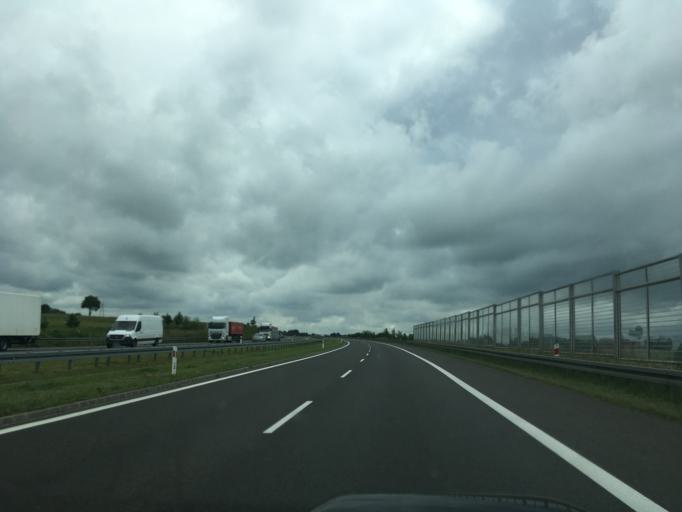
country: PL
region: Lublin Voivodeship
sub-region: Powiat lubelski
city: Jastkow
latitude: 51.2962
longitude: 22.4062
